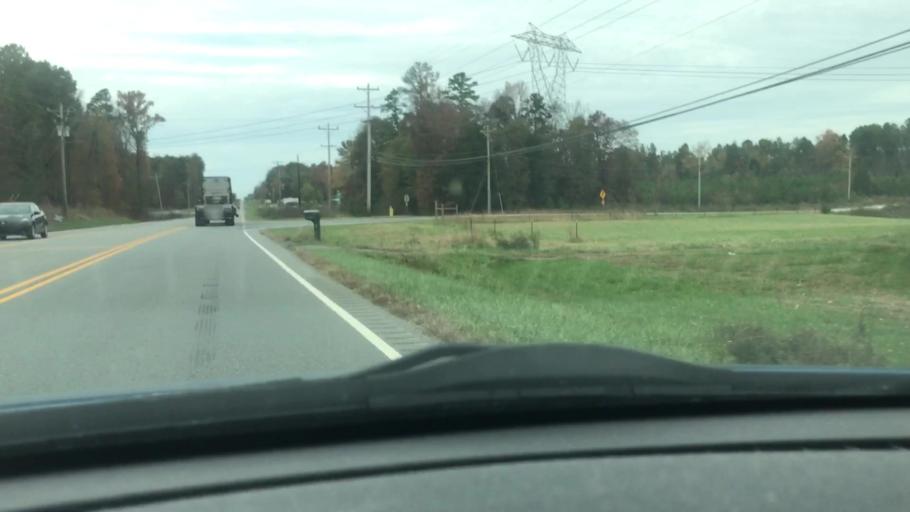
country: US
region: North Carolina
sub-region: Davidson County
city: Thomasville
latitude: 35.7796
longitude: -80.1212
